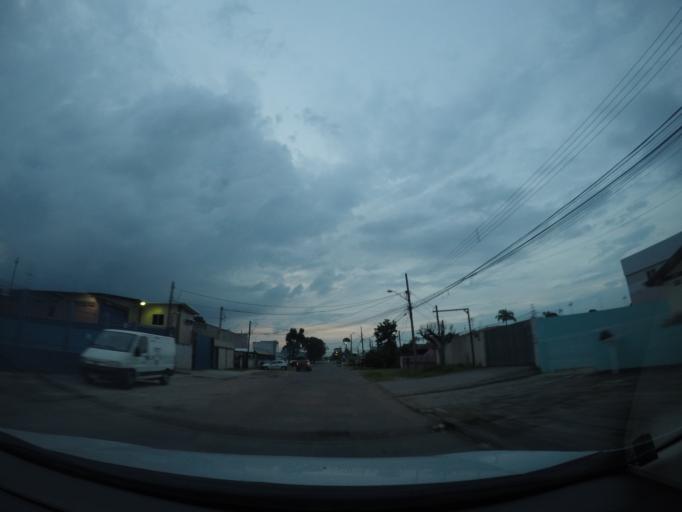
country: BR
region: Parana
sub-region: Sao Jose Dos Pinhais
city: Sao Jose dos Pinhais
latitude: -25.4976
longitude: -49.2312
